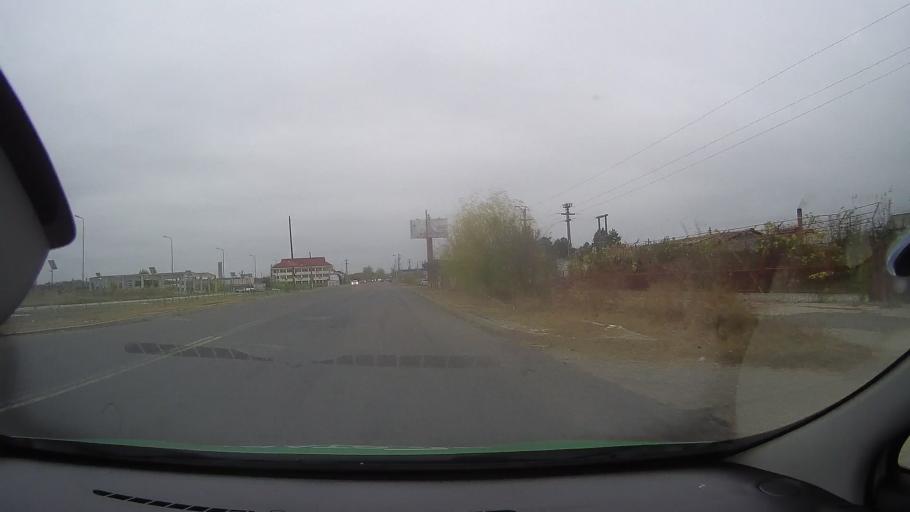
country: RO
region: Ialomita
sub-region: Comuna Slobozia
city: Slobozia
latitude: 44.5813
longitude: 27.3879
